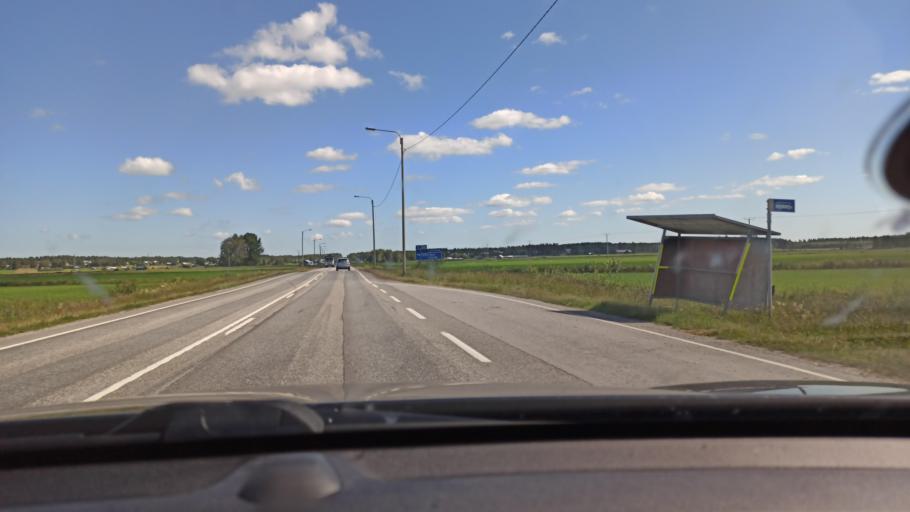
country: FI
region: Ostrobothnia
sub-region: Vaasa
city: Teeriniemi
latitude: 63.0017
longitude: 21.6737
